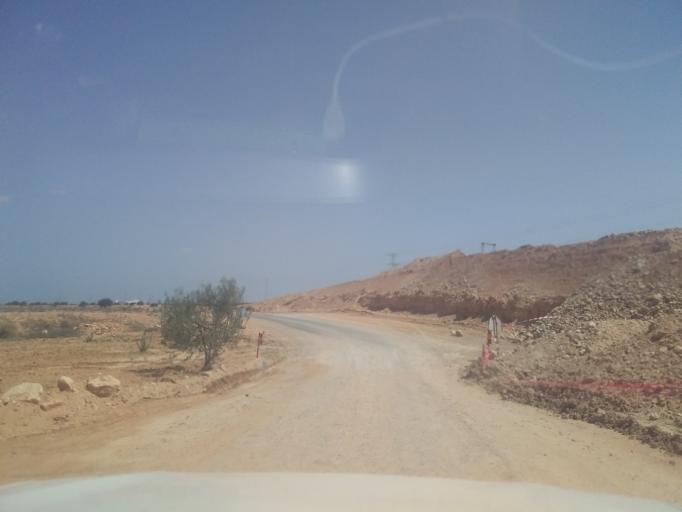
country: TN
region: Qabis
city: Matmata
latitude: 33.6063
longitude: 10.2022
